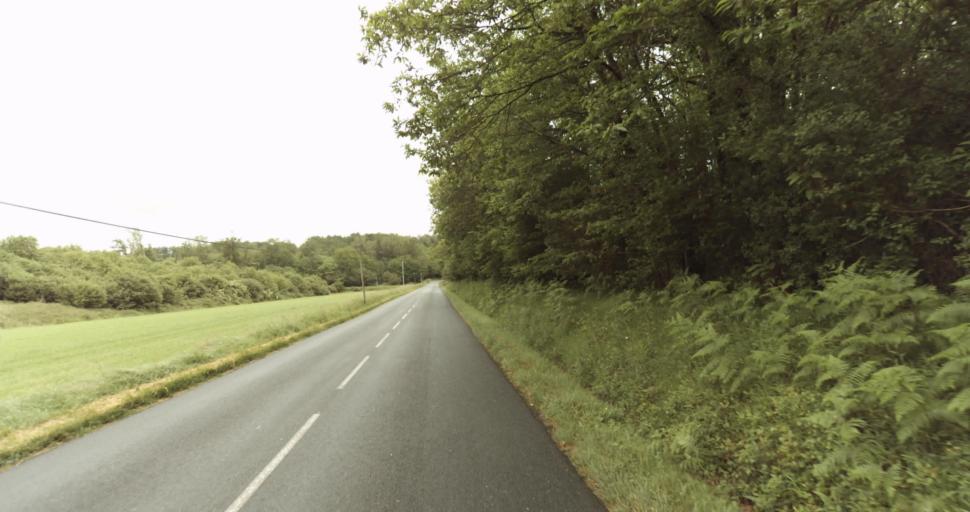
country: FR
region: Aquitaine
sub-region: Departement de la Dordogne
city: Belves
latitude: 44.7153
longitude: 0.9352
